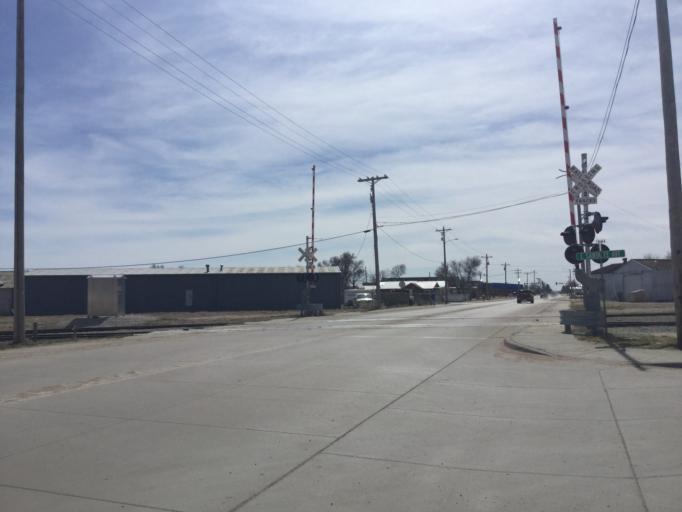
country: US
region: Kansas
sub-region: Grant County
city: Ulysses
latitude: 37.5793
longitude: -101.3545
